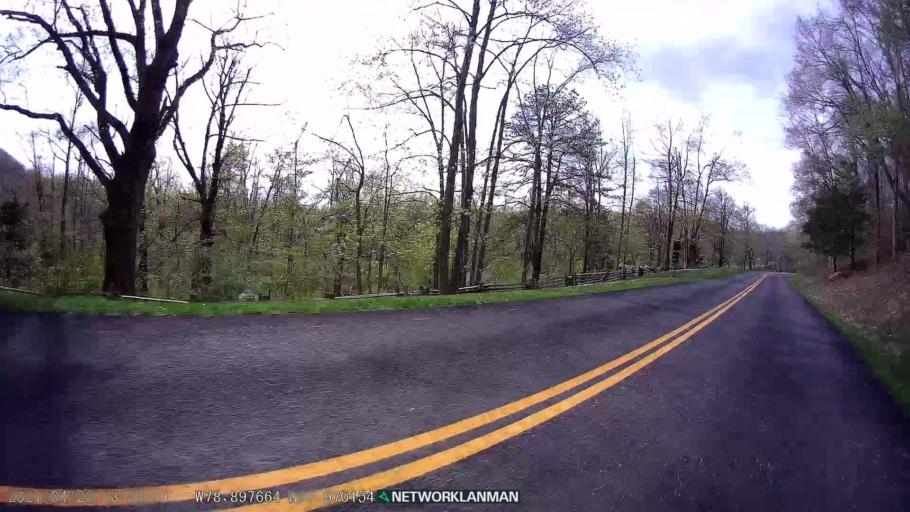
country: US
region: Virginia
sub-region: Augusta County
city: Lyndhurst
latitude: 37.9701
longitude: -78.8975
